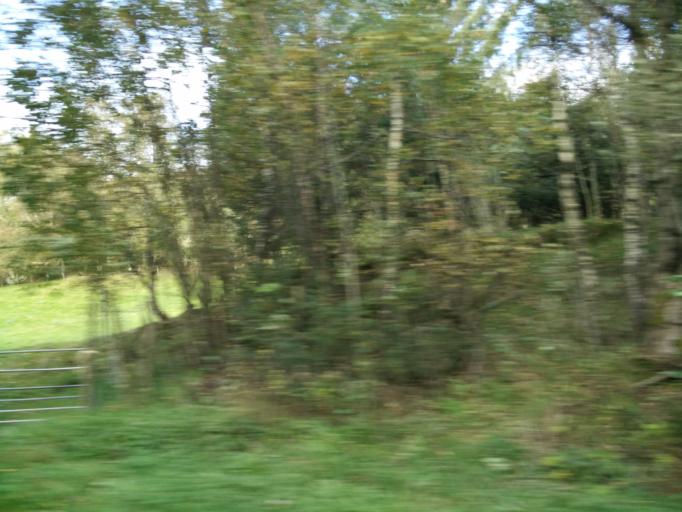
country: NO
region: Hordaland
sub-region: Sveio
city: Sveio
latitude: 59.5451
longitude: 5.3402
